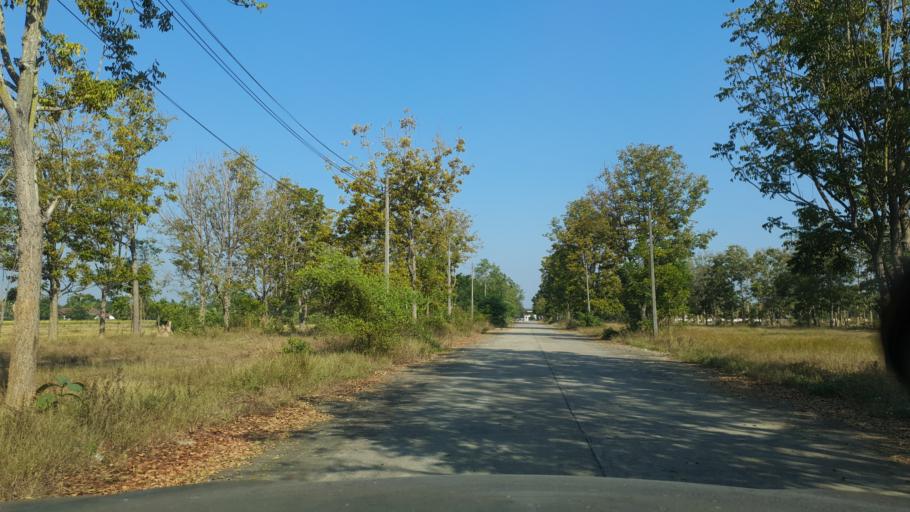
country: TH
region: Lamphun
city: Ban Thi
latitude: 18.6792
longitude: 99.1235
